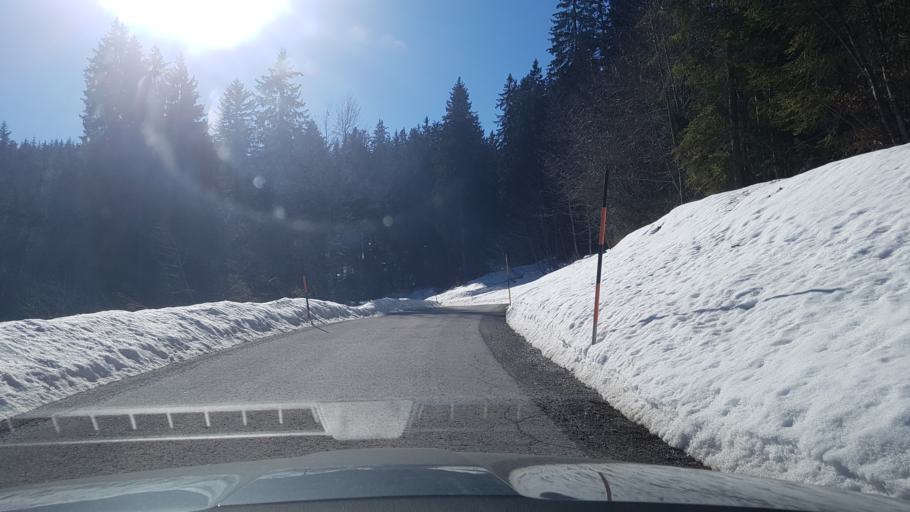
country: AT
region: Salzburg
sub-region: Politischer Bezirk Hallein
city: Abtenau
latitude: 47.6157
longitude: 13.3833
